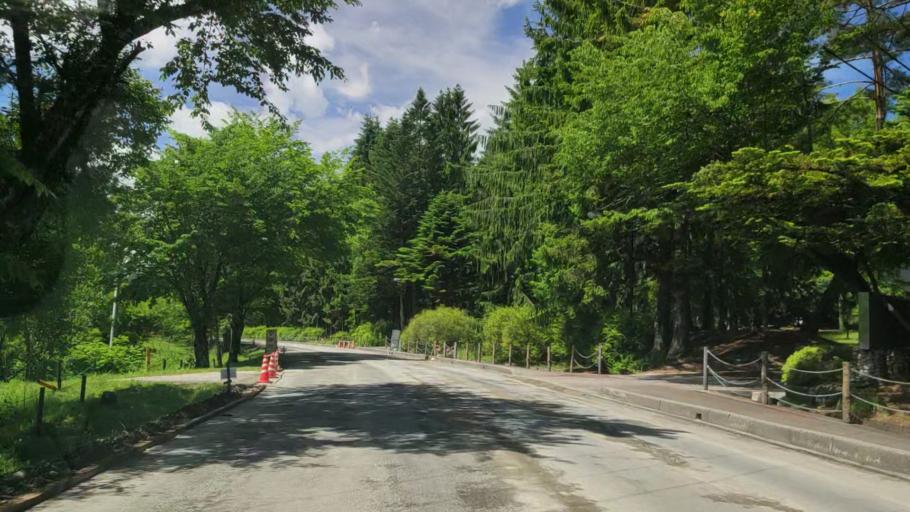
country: JP
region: Nagano
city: Chino
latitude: 36.0486
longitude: 138.2500
